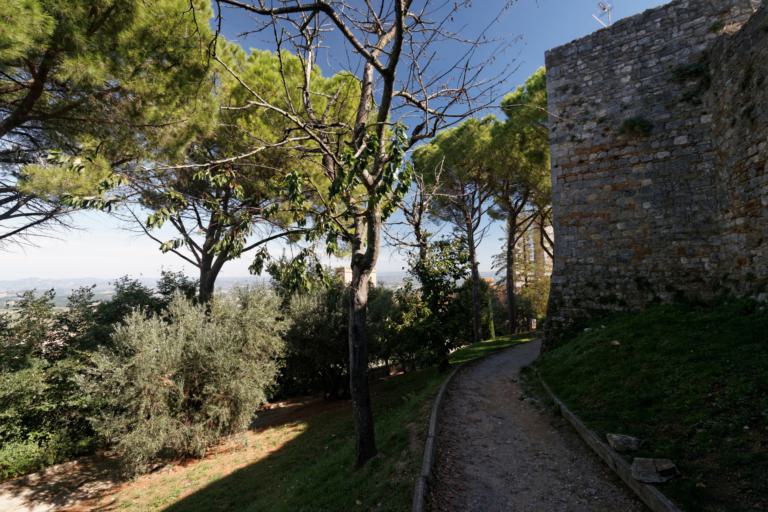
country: IT
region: Tuscany
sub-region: Provincia di Siena
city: San Gimignano
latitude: 43.4682
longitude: 11.0414
